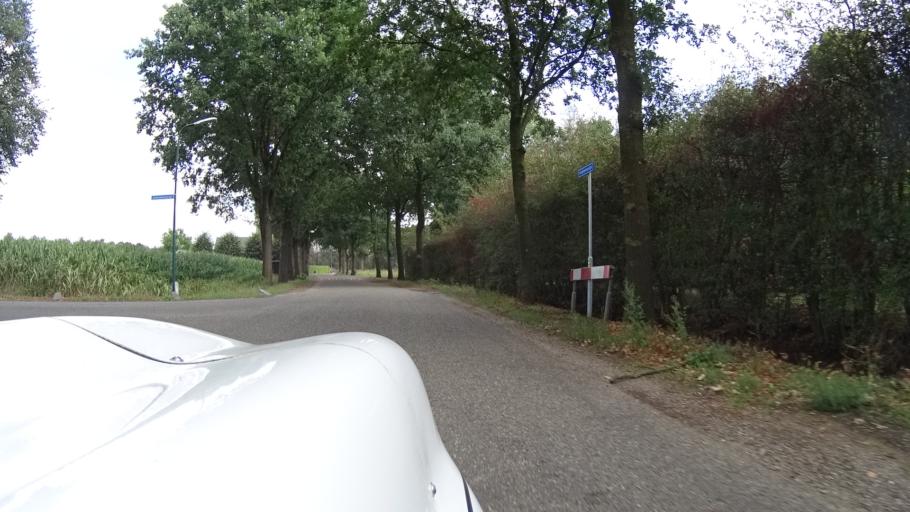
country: NL
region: North Brabant
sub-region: Gemeente Bernheze
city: Loosbroek
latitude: 51.6694
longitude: 5.4905
